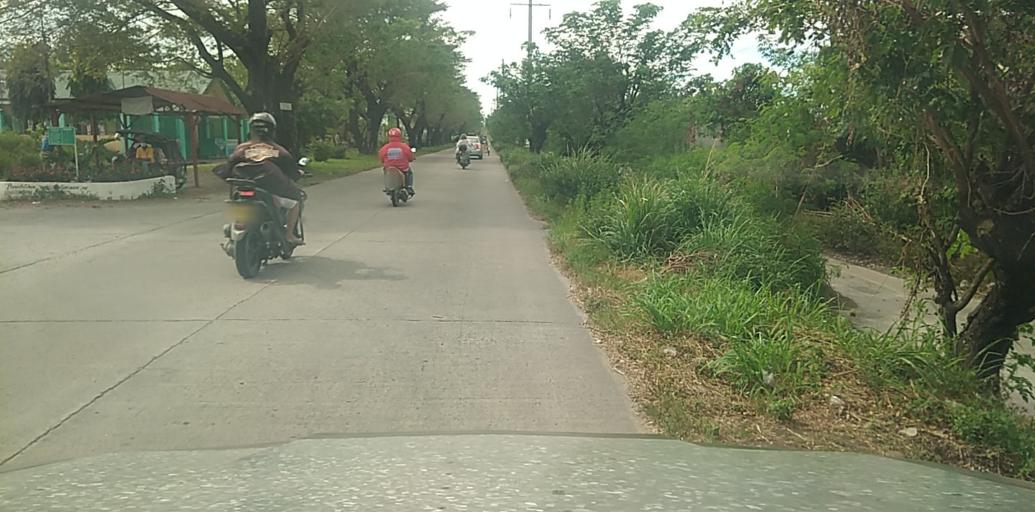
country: PH
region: Central Luzon
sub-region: Province of Pampanga
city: Pandacaqui
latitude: 15.1775
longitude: 120.6608
